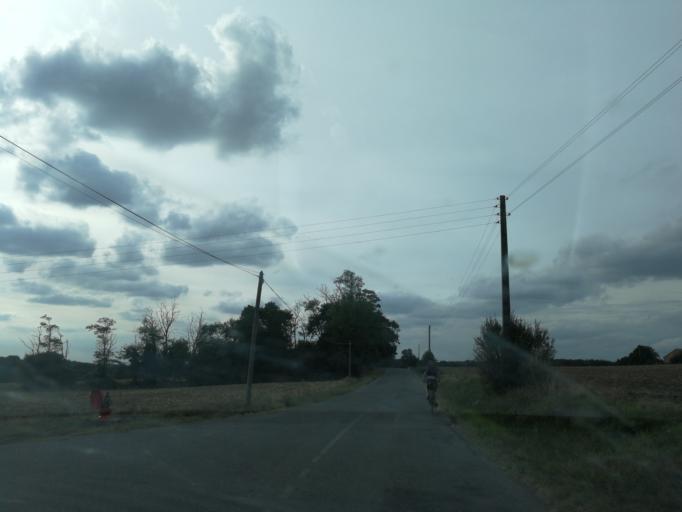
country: FR
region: Midi-Pyrenees
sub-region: Departement de la Haute-Garonne
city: Flourens
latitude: 43.6019
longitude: 1.5406
